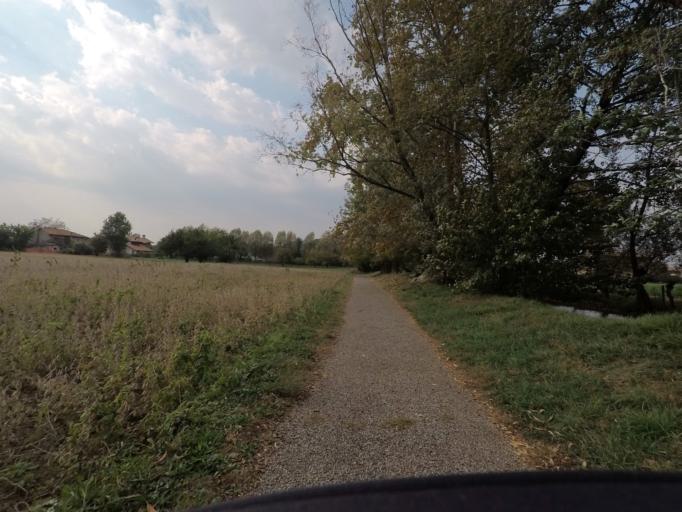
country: IT
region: Friuli Venezia Giulia
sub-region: Provincia di Udine
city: Tavagnacco
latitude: 46.1145
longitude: 13.2412
